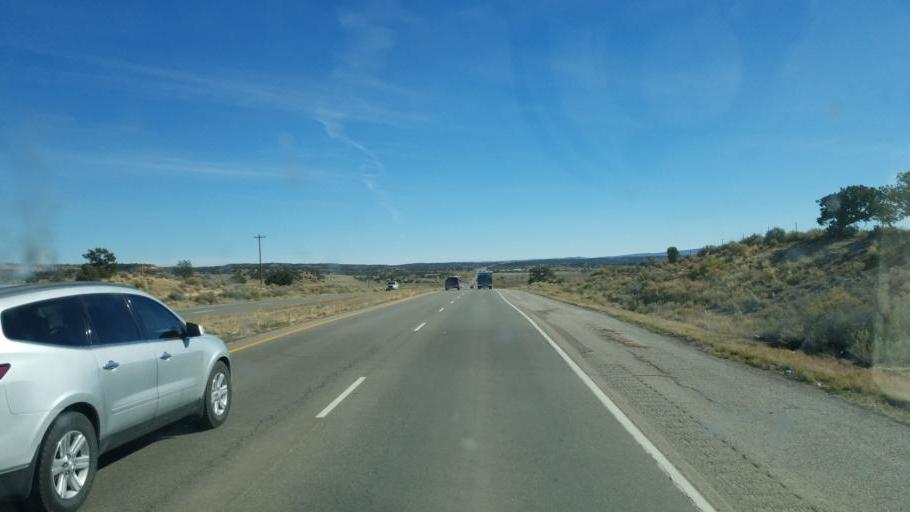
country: US
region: Arizona
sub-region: Apache County
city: Window Rock
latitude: 35.6269
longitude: -108.9366
